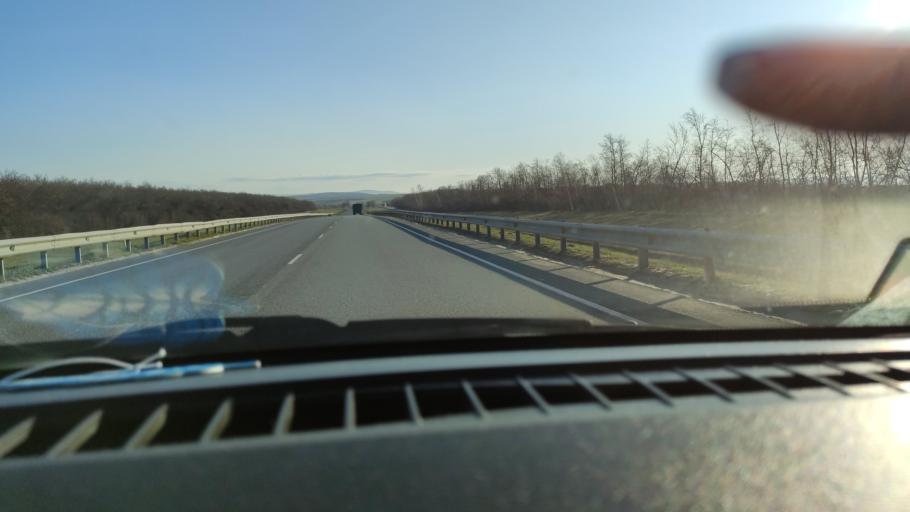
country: RU
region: Saratov
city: Balakovo
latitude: 52.1035
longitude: 47.7394
